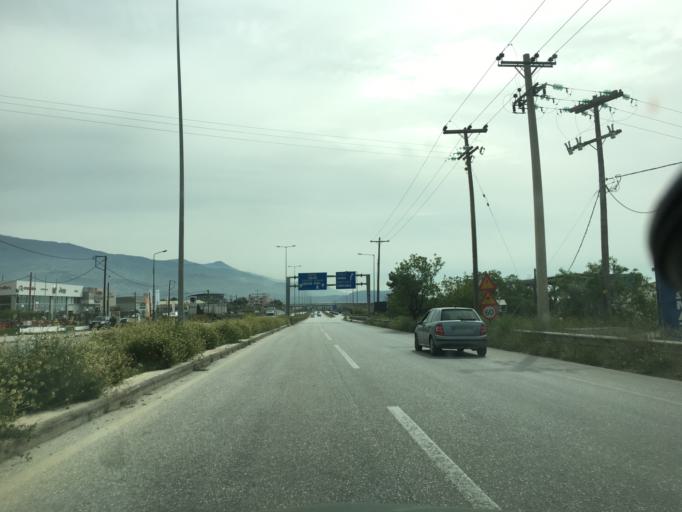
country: GR
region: Thessaly
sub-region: Nomos Magnisias
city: Nea Ionia
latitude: 39.3756
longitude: 22.8958
